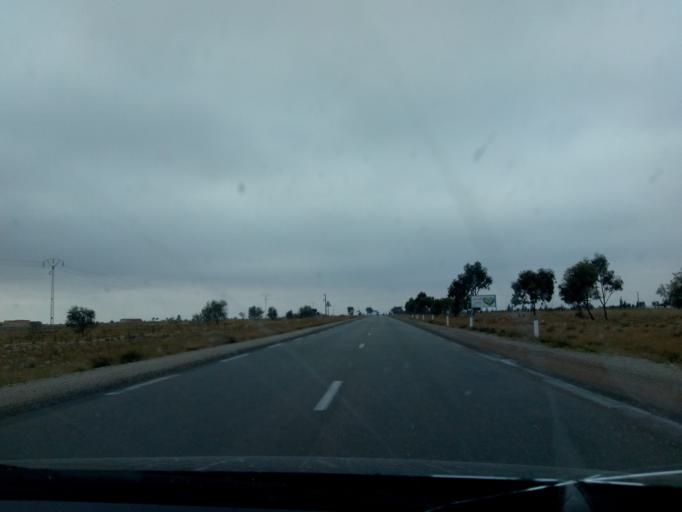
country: TN
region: Madanin
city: Medenine
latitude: 33.2787
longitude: 10.4693
